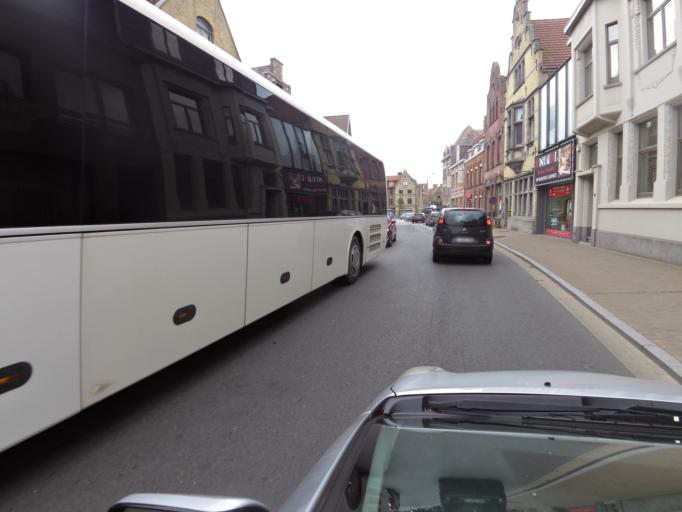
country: BE
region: Flanders
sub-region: Provincie West-Vlaanderen
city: Diksmuide
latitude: 51.0327
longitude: 2.8661
